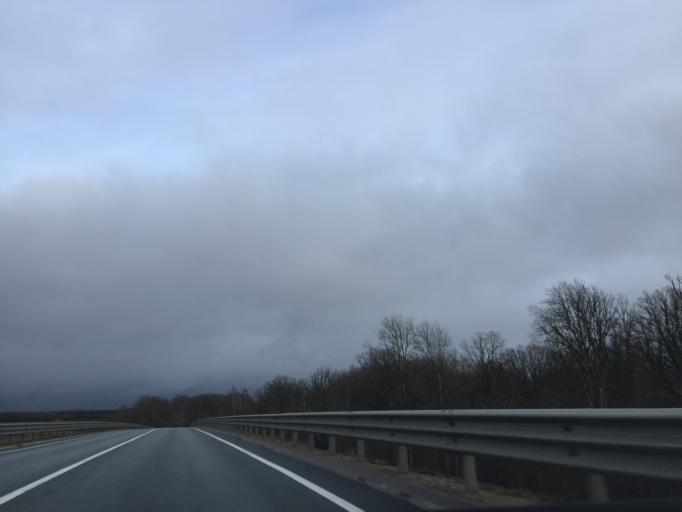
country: LV
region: Engure
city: Smarde
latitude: 56.7809
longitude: 23.3707
